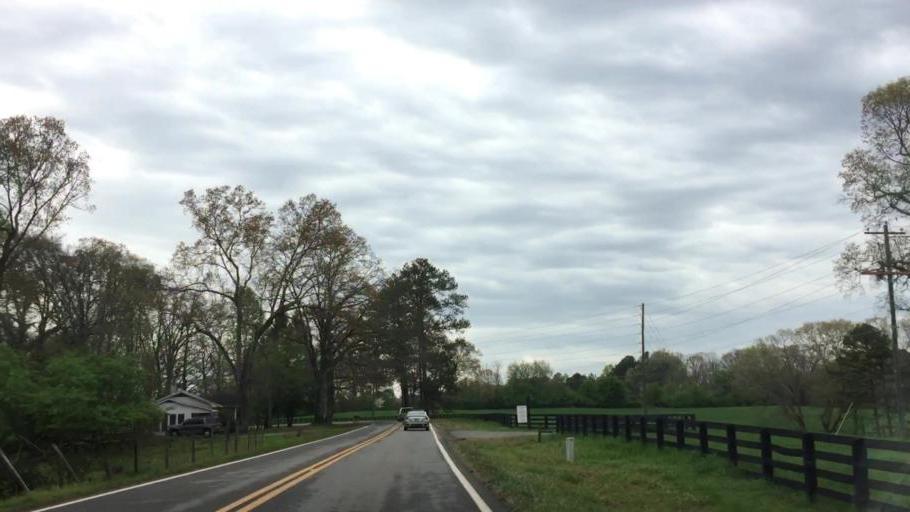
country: US
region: Georgia
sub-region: Fulton County
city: Milton
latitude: 34.1859
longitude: -84.3407
